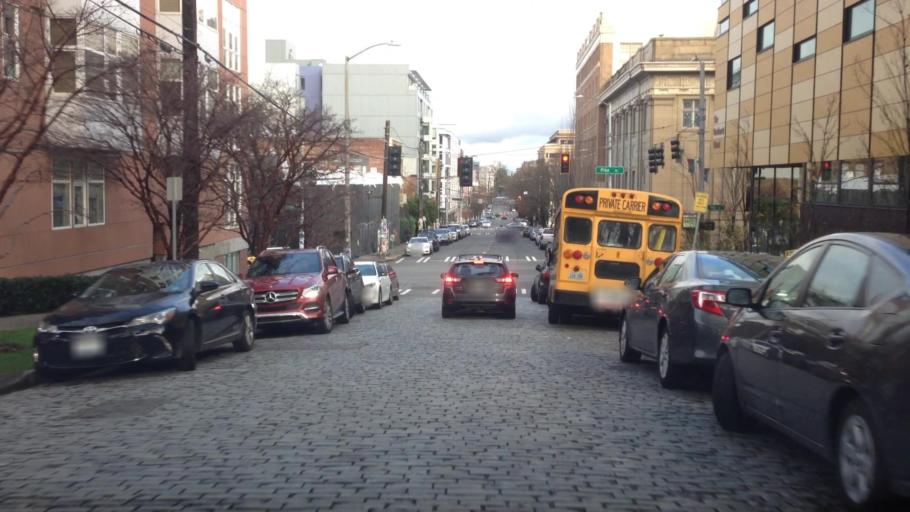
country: US
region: Washington
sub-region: King County
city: Seattle
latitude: 47.6136
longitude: -122.3268
